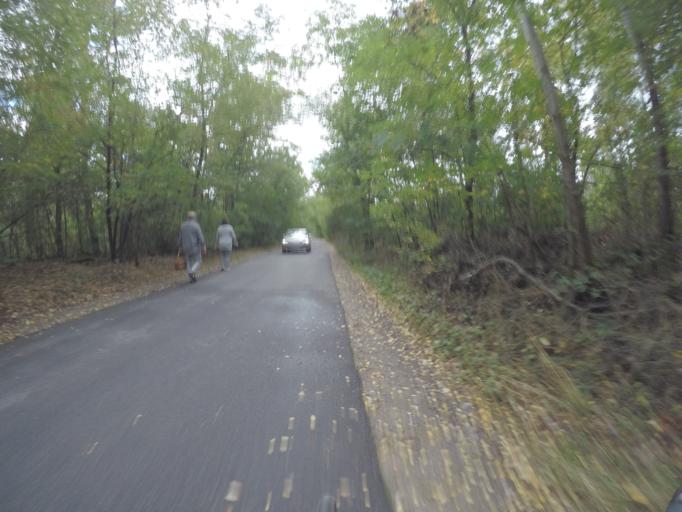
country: DE
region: Brandenburg
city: Strausberg
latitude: 52.6003
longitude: 13.9069
